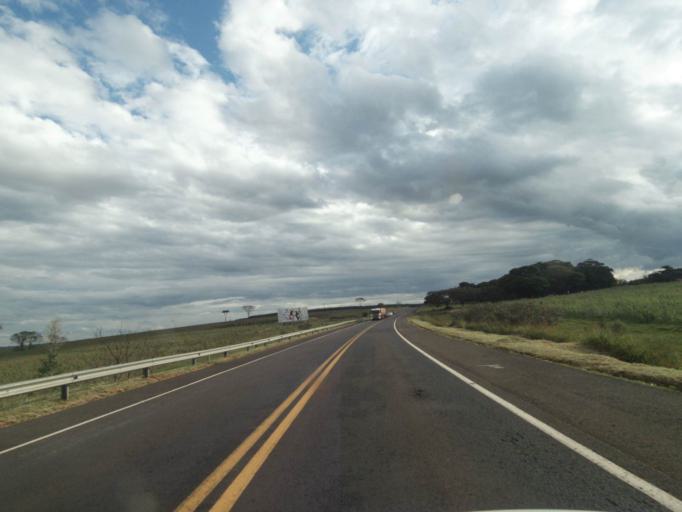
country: PY
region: Canindeyu
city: Salto del Guaira
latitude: -24.0830
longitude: -54.0690
